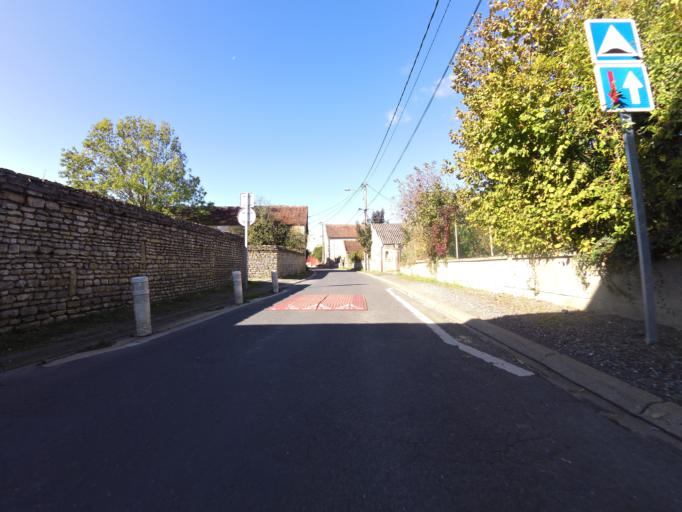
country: FR
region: Lower Normandy
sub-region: Departement du Calvados
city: Canon
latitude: 49.0477
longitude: -0.1310
